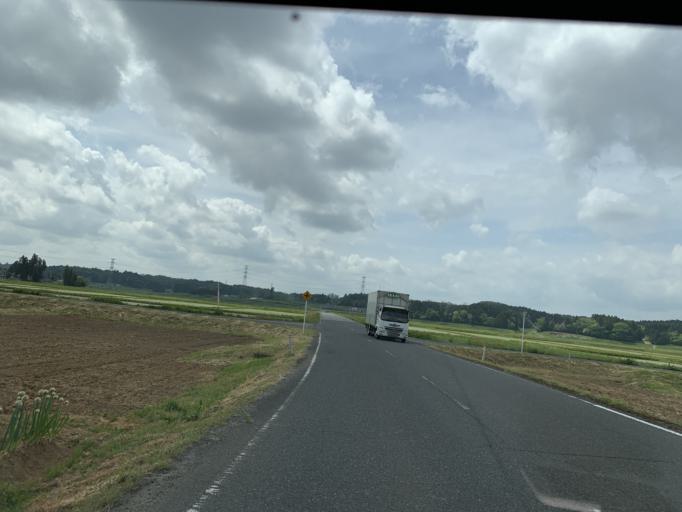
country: JP
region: Iwate
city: Ichinoseki
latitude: 38.8243
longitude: 141.0205
